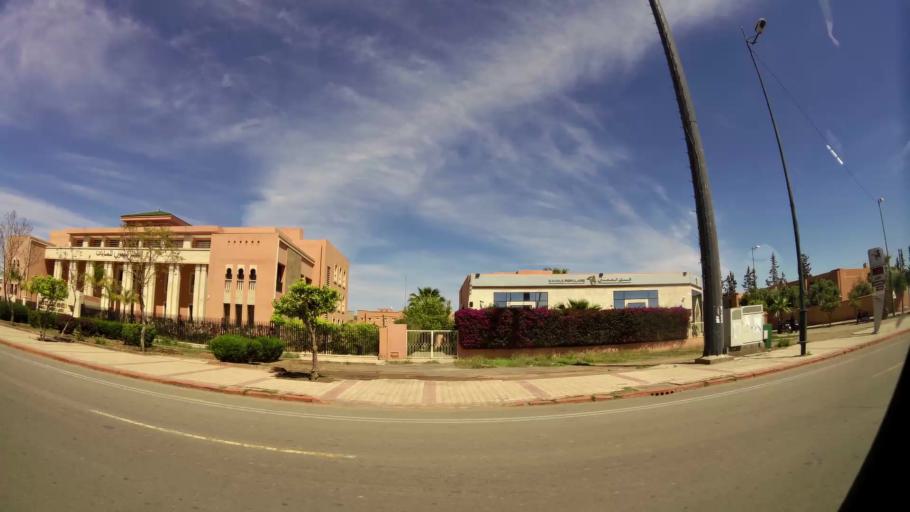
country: MA
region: Marrakech-Tensift-Al Haouz
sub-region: Marrakech
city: Marrakesh
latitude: 31.6101
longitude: -7.9739
